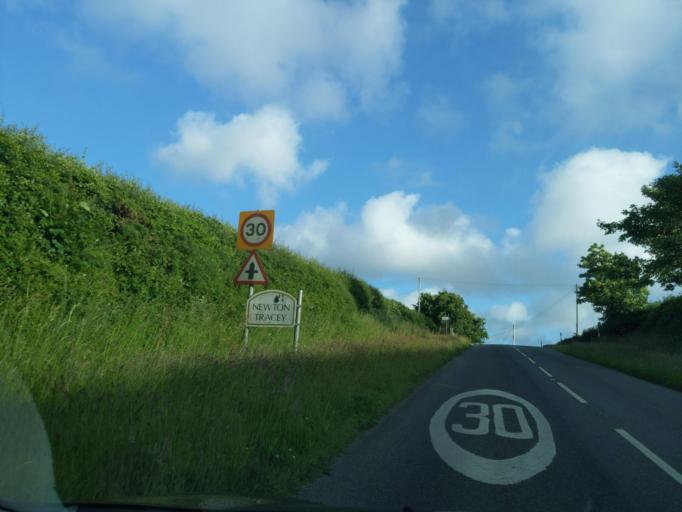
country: GB
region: England
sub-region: Devon
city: Fremington
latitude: 51.0281
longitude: -4.1015
